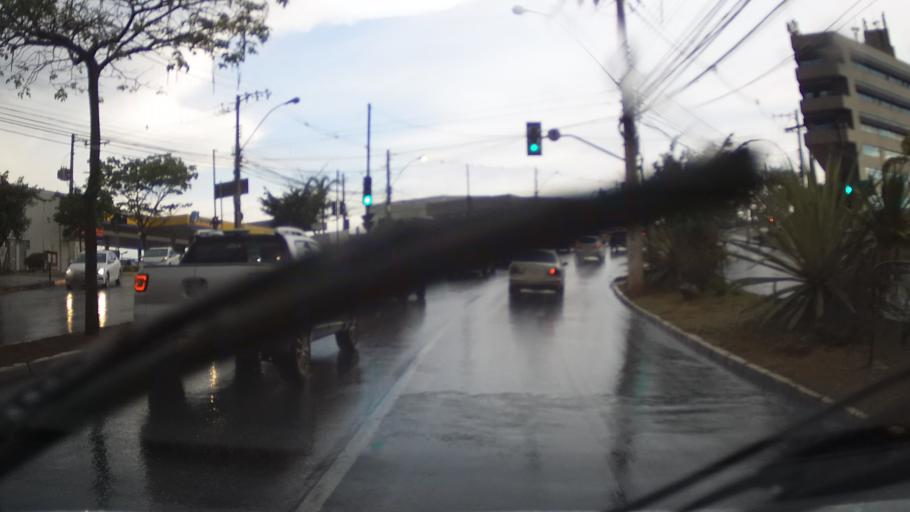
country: BR
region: Minas Gerais
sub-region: Belo Horizonte
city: Belo Horizonte
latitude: -19.9575
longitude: -43.9572
